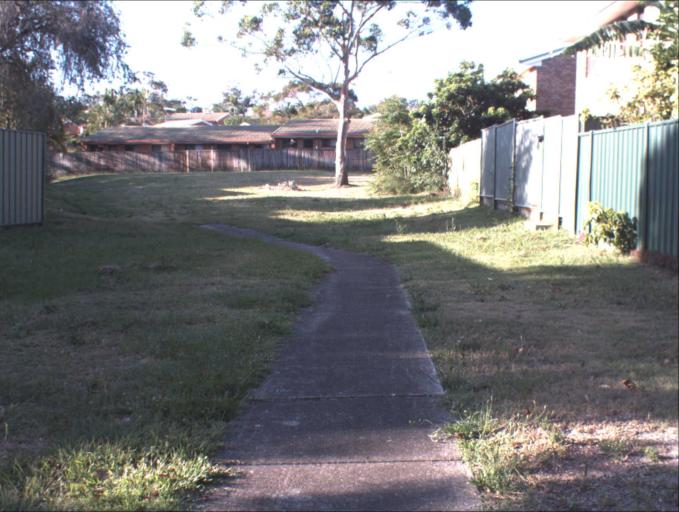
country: AU
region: Queensland
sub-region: Logan
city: Springwood
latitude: -27.6082
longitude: 153.1230
